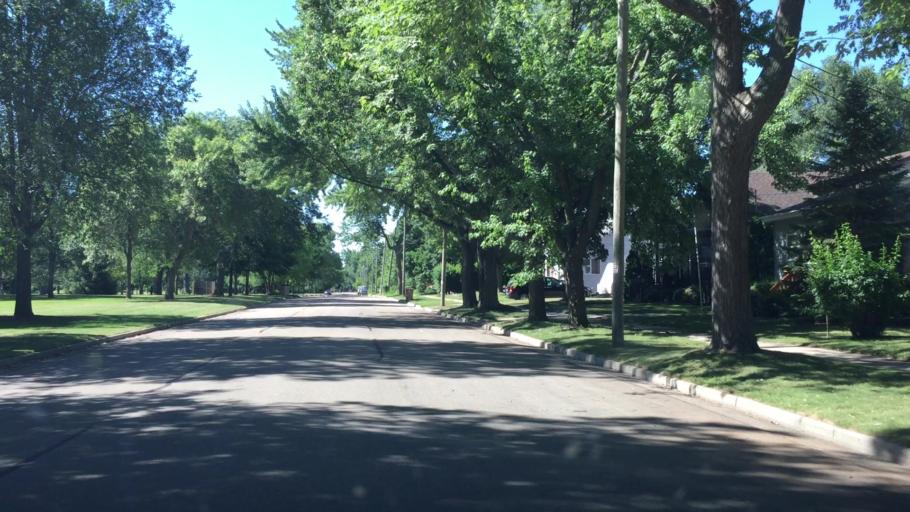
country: US
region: Wisconsin
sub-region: Winnebago County
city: Menasha
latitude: 44.1980
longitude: -88.4420
